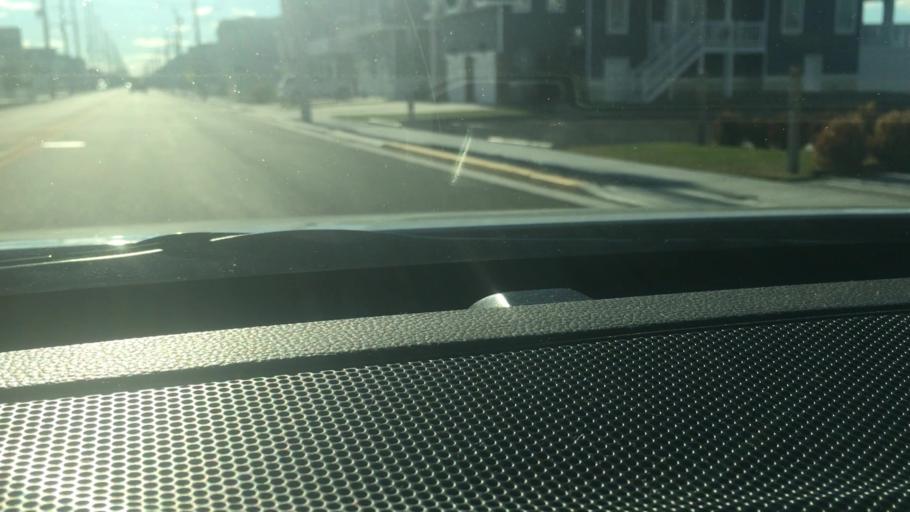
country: US
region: New Jersey
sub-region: Cape May County
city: Avalon
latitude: 39.0959
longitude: -74.7259
